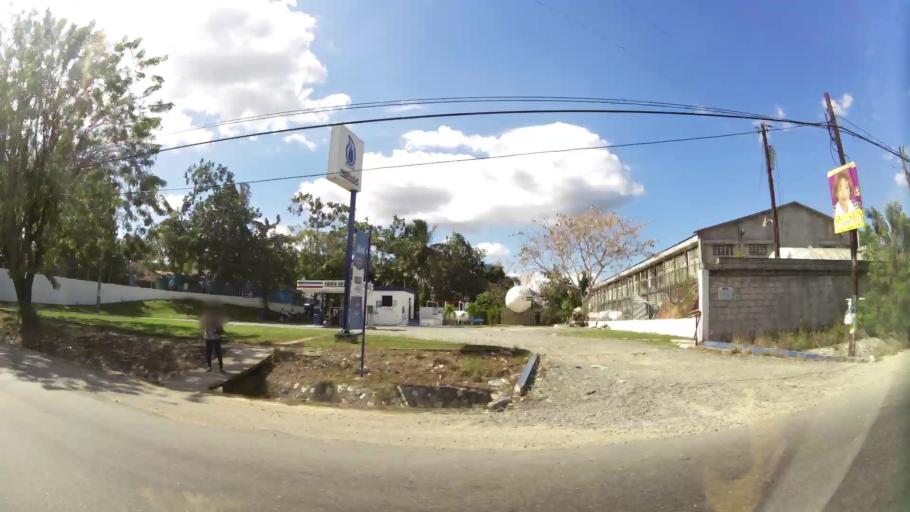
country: DO
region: San Cristobal
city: San Cristobal
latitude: 18.4257
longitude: -70.0680
